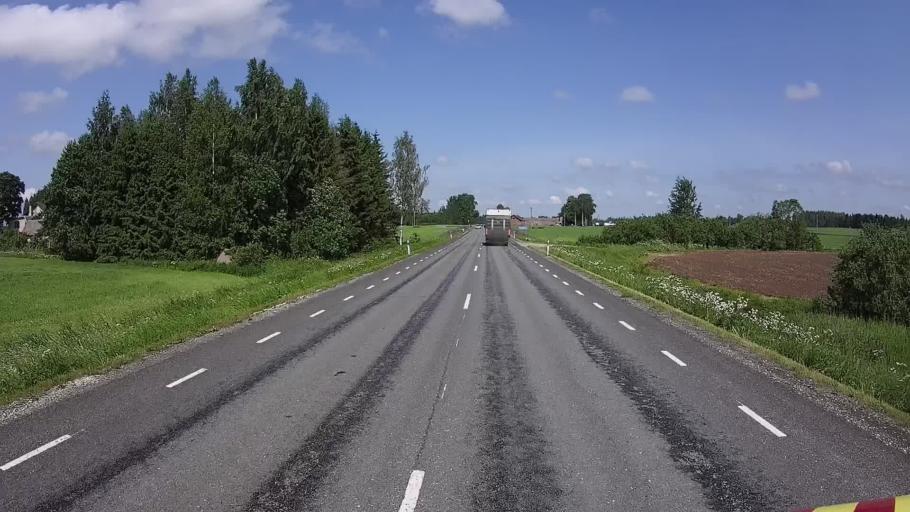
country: EE
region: Tartu
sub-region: UElenurme vald
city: Ulenurme
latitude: 58.2012
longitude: 26.8114
